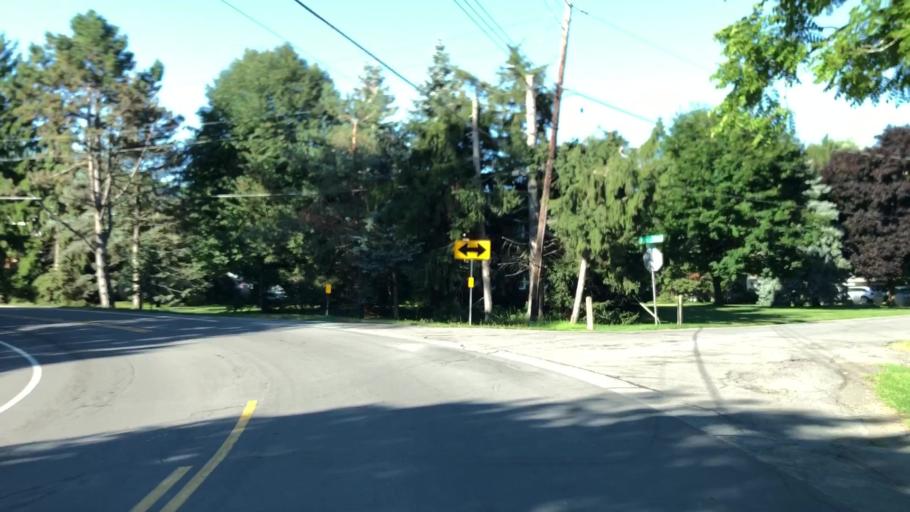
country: US
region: New York
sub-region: Erie County
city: Depew
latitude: 42.8542
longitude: -78.7006
